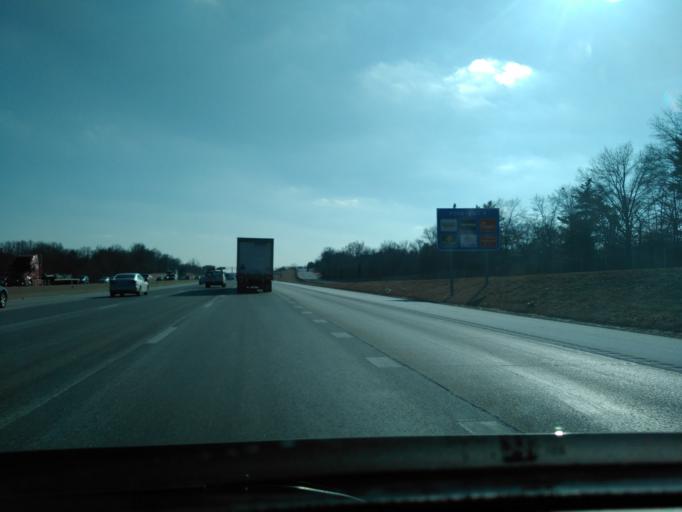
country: US
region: Missouri
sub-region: Saint Louis County
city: Town and Country
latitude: 38.6243
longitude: -90.4514
